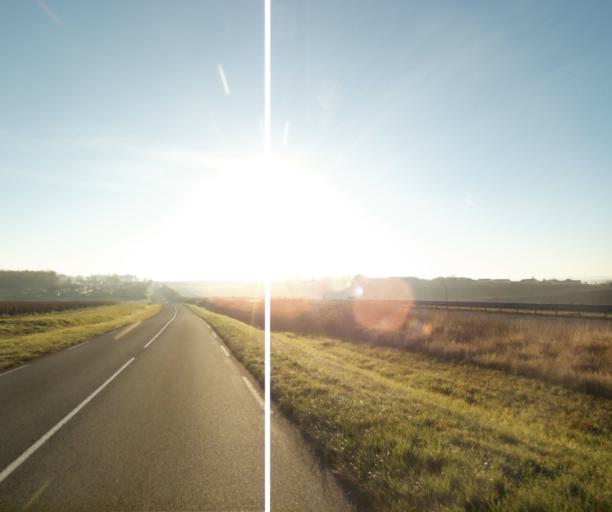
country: FR
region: Poitou-Charentes
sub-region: Departement de la Charente-Maritime
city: Cherac
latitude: 45.7037
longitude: -0.4732
